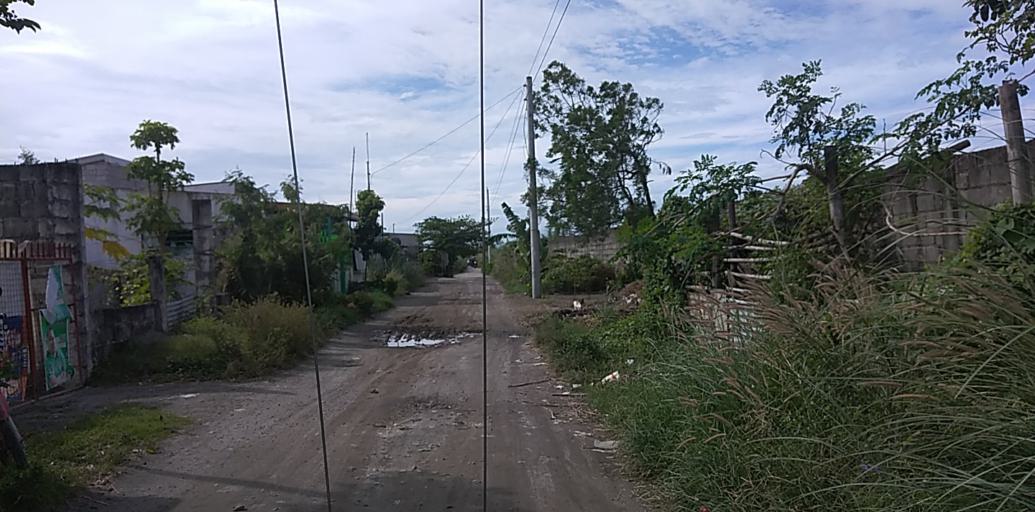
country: PH
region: Central Luzon
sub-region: Province of Pampanga
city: Manibaug Pasig
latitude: 15.1290
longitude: 120.5553
